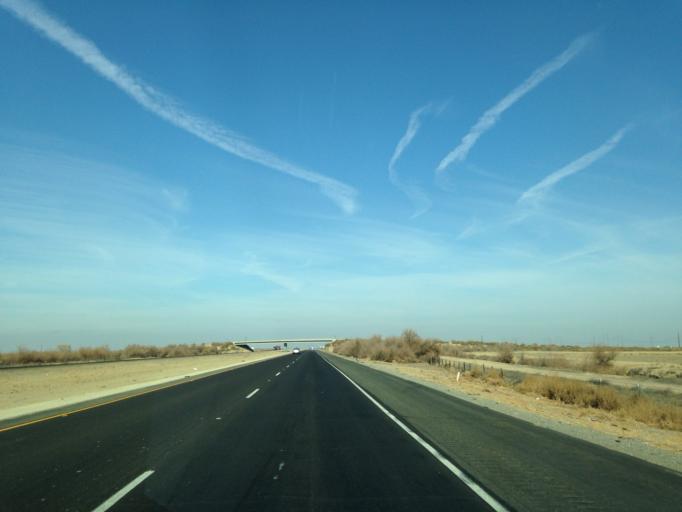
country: US
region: California
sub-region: Kern County
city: Lost Hills
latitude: 35.7863
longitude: -119.7797
